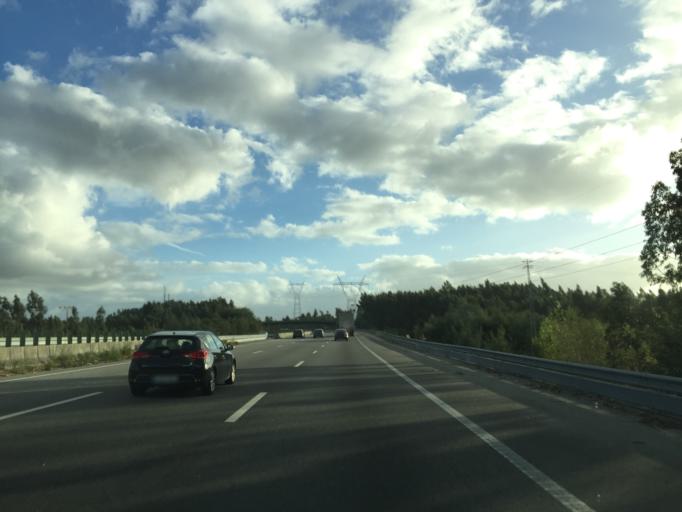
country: PT
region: Coimbra
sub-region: Condeixa-A-Nova
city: Condeixa-a-Nova
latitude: 40.1797
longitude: -8.4931
